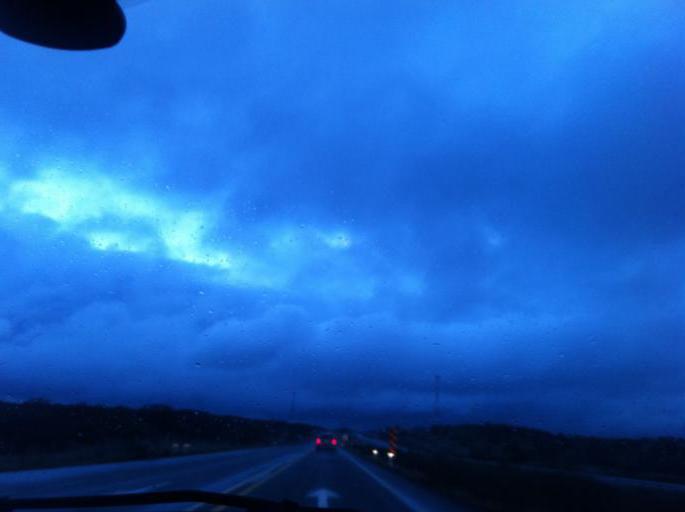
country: MX
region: Sonora
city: Benjamin Hill
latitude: 29.9029
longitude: -111.1045
